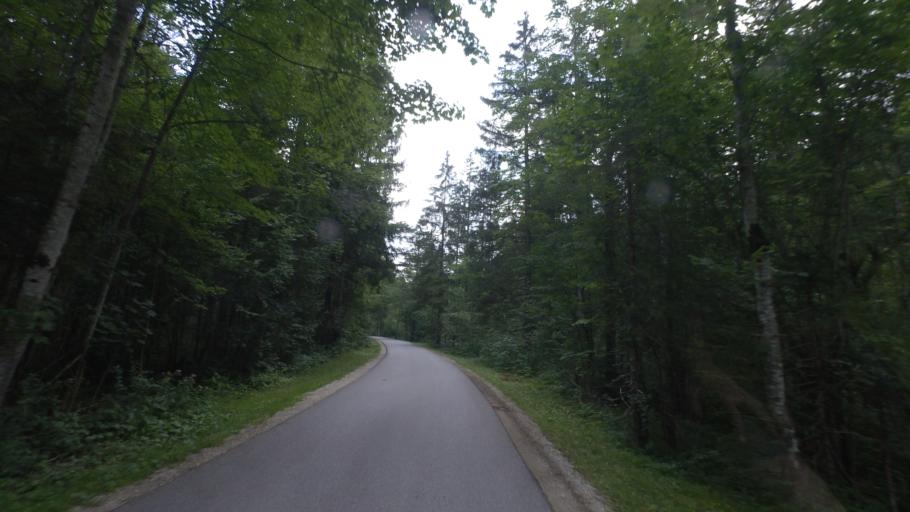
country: DE
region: Bavaria
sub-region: Upper Bavaria
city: Ruhpolding
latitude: 47.7289
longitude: 12.5854
